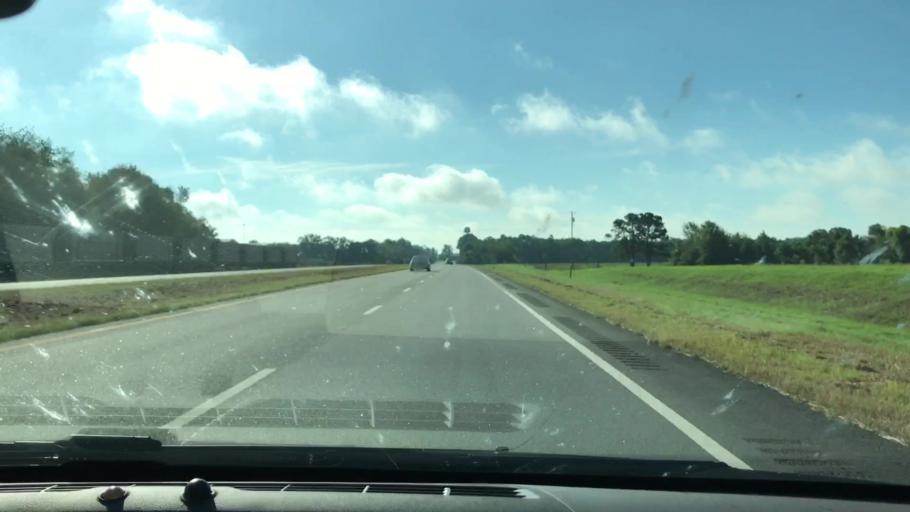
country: US
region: Georgia
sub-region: Terrell County
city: Dawson
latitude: 31.7266
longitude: -84.3590
